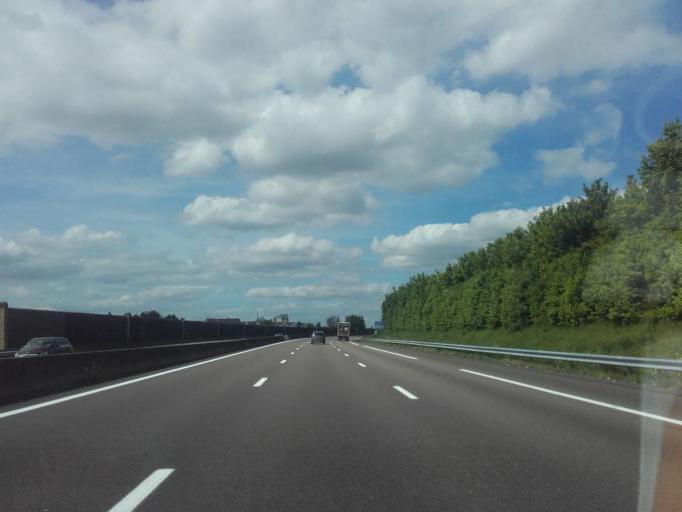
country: FR
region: Bourgogne
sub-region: Departement de Saone-et-Loire
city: Saint-Remy
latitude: 46.7705
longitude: 4.8211
